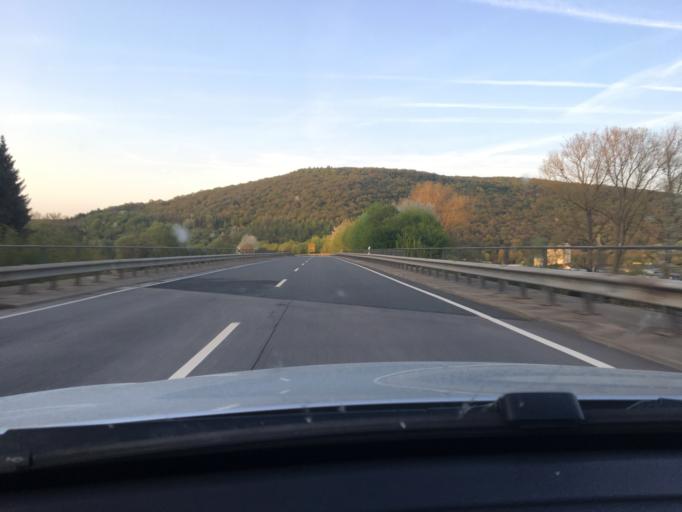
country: DE
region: Rheinland-Pfalz
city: Katzenbach
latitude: 49.6412
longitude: 7.8233
